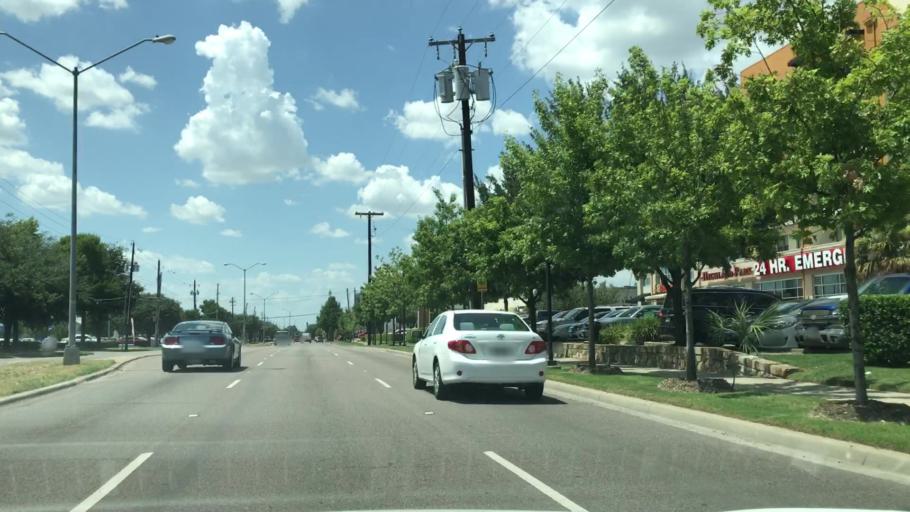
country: US
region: Texas
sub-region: Dallas County
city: Highland Park
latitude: 32.8246
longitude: -96.8203
